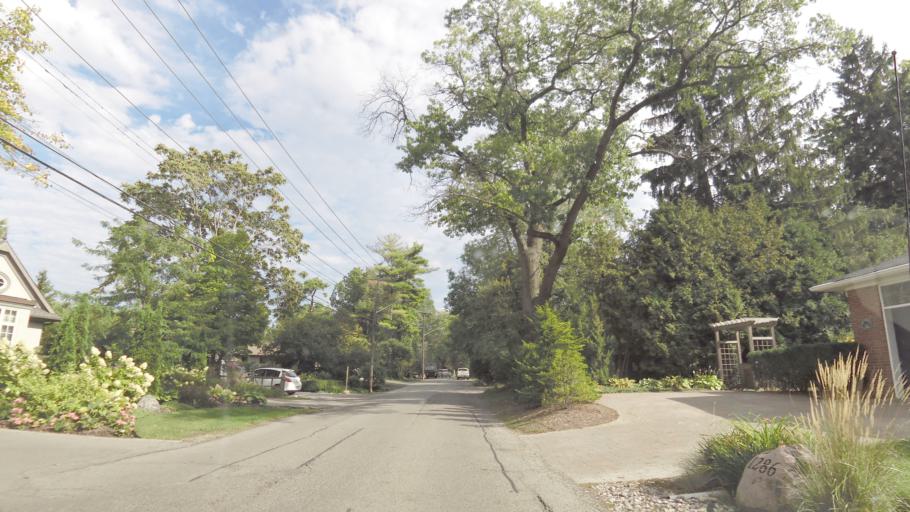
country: CA
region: Ontario
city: Mississauga
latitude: 43.5544
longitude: -79.5970
